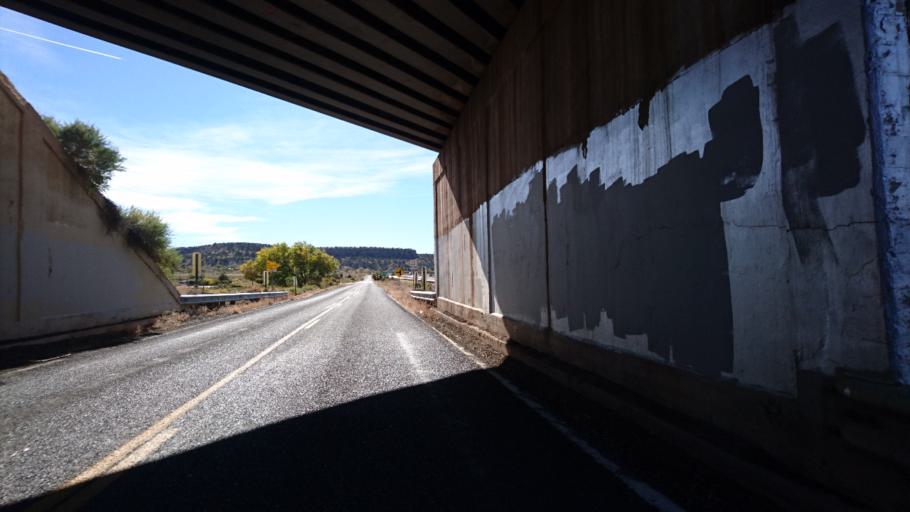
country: US
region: New Mexico
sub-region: Cibola County
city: Skyline-Ganipa
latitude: 35.0665
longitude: -107.6852
